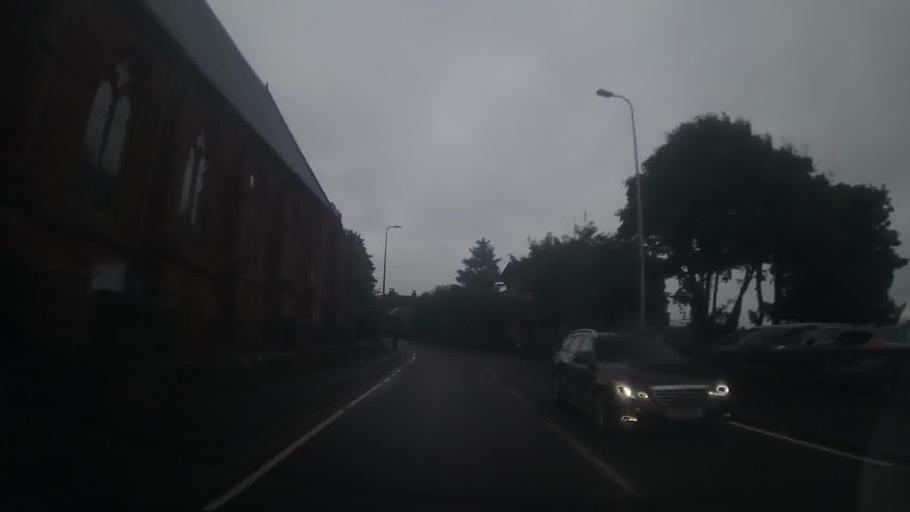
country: GB
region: Scotland
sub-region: Inverclyde
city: Wemyss Bay
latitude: 55.8723
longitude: -4.8910
